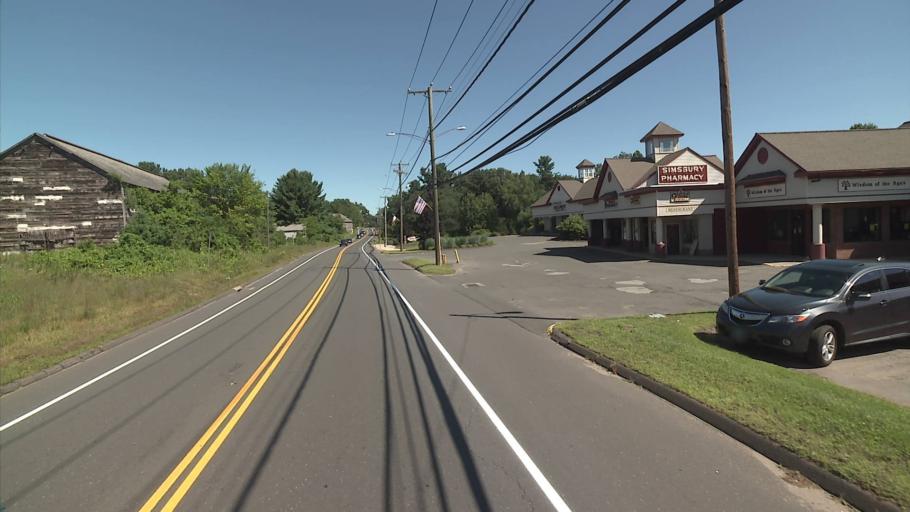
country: US
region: Connecticut
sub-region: Hartford County
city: Tariffville
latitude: 41.9041
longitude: -72.7864
